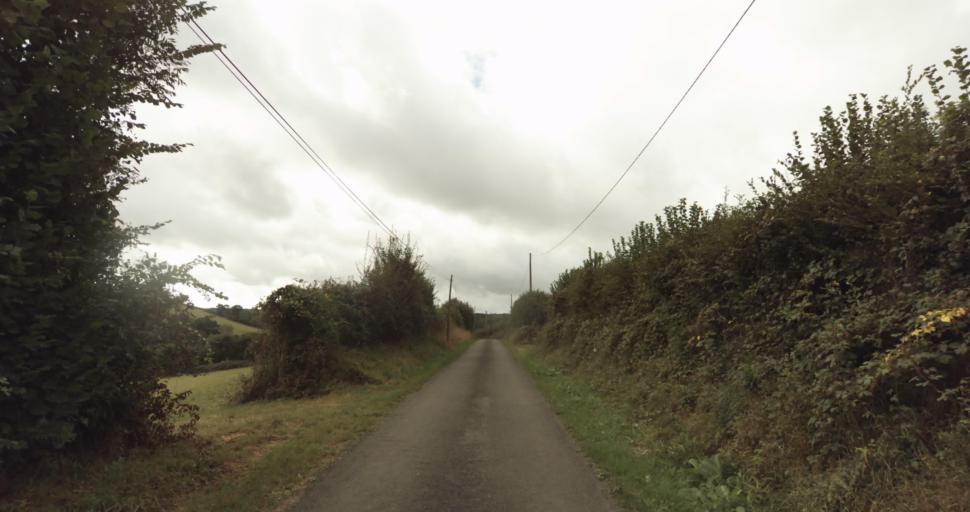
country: FR
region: Lower Normandy
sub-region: Departement de l'Orne
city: Gace
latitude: 48.8569
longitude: 0.2842
